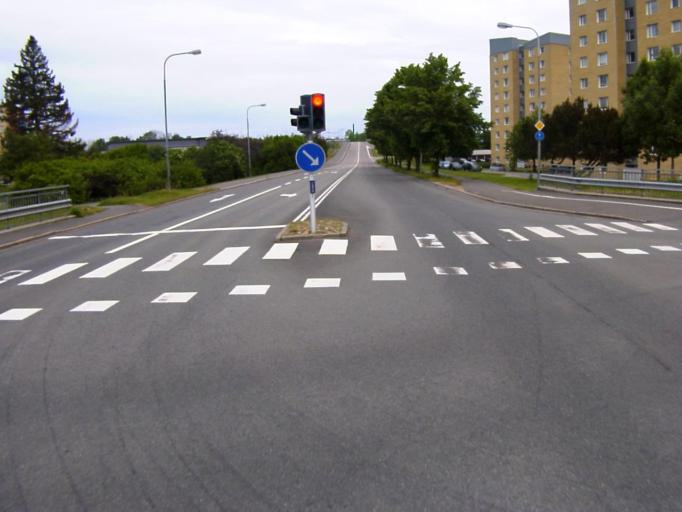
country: SE
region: Skane
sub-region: Kristianstads Kommun
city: Kristianstad
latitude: 56.0394
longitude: 14.1619
